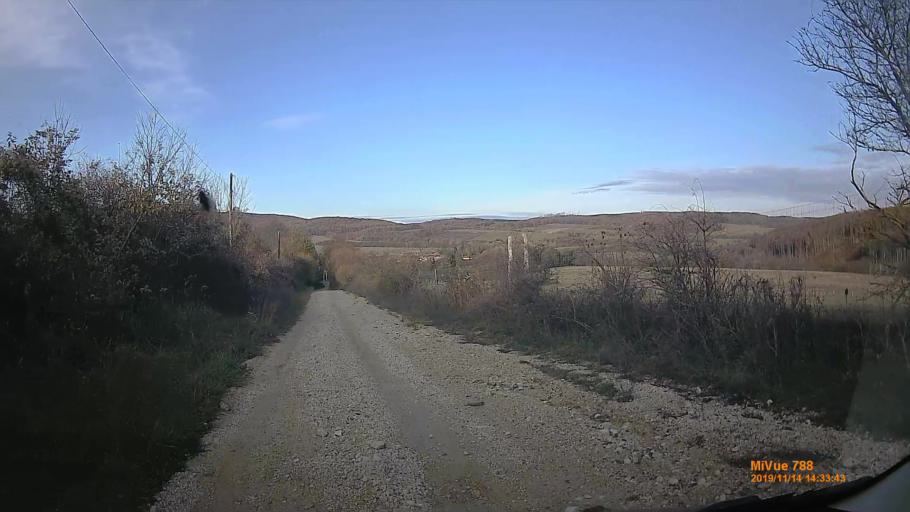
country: HU
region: Veszprem
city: Zirc
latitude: 47.2202
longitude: 17.7895
